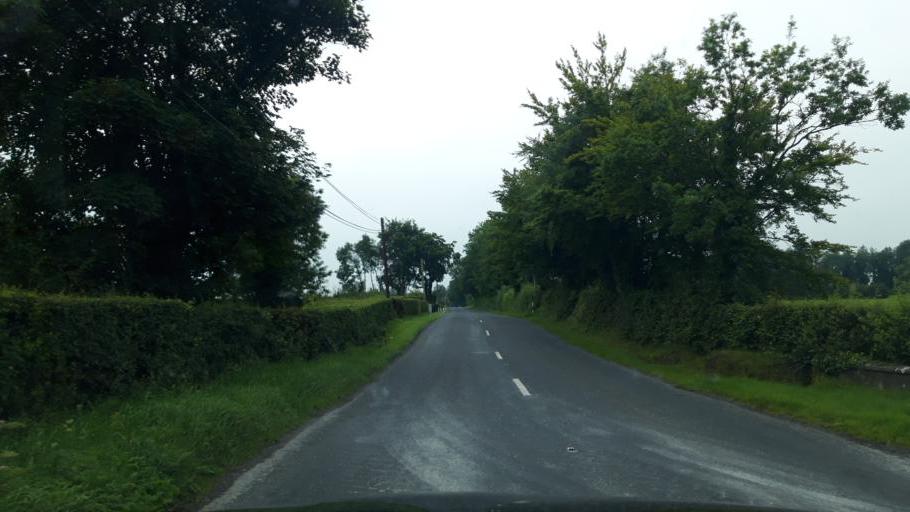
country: IE
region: Munster
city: Fethard
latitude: 52.5470
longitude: -7.6786
